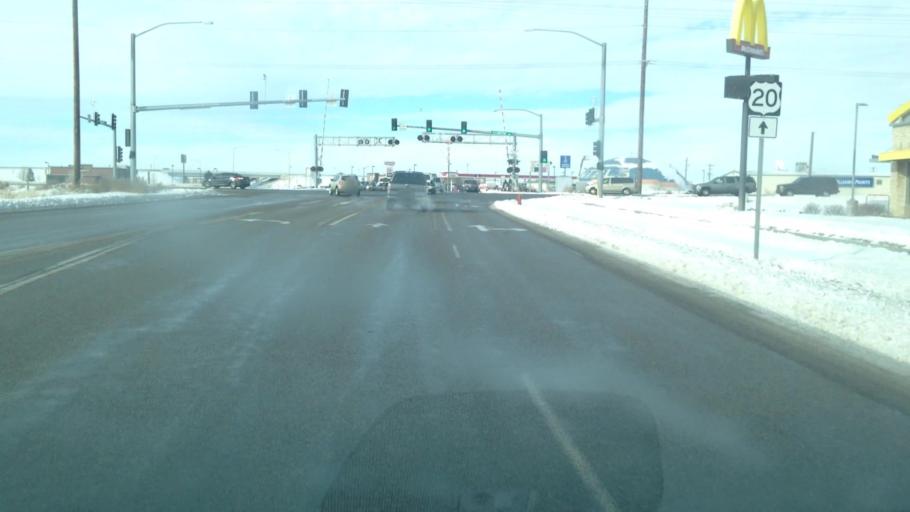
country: US
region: Idaho
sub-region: Madison County
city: Rexburg
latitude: 43.8036
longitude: -111.8078
